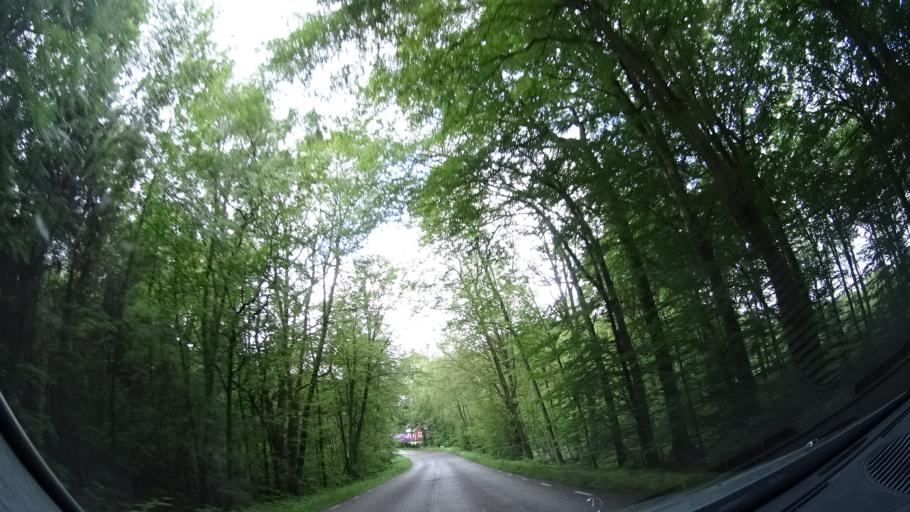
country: SE
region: Skane
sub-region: Hoors Kommun
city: Hoeoer
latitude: 55.9565
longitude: 13.4533
